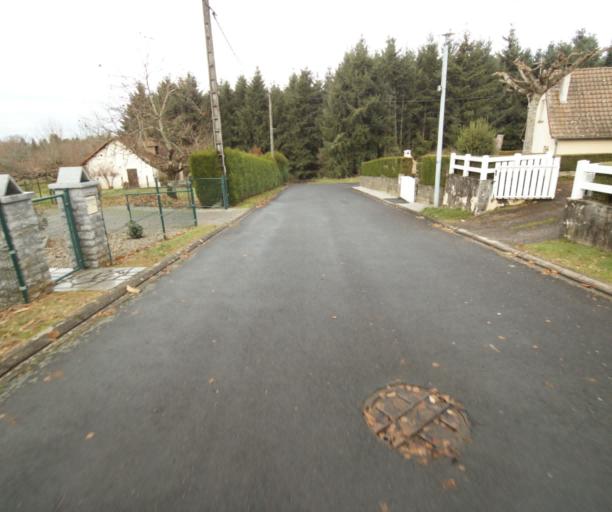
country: FR
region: Limousin
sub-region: Departement de la Correze
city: Saint-Mexant
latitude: 45.2655
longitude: 1.6360
